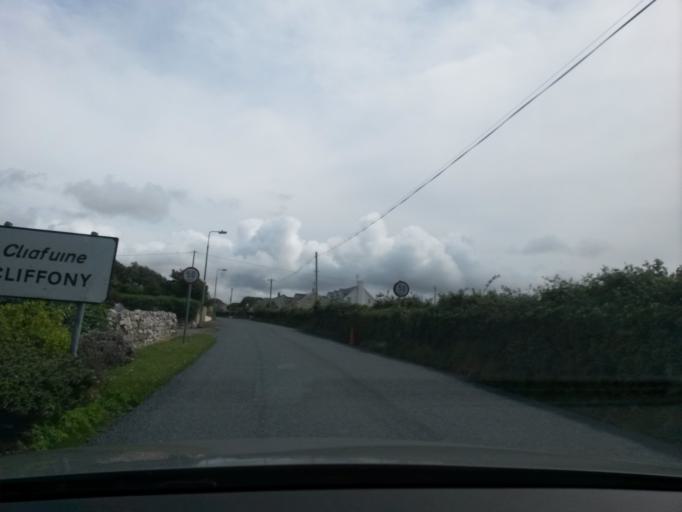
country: IE
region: Connaught
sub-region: Sligo
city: Sligo
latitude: 54.4325
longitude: -8.4567
